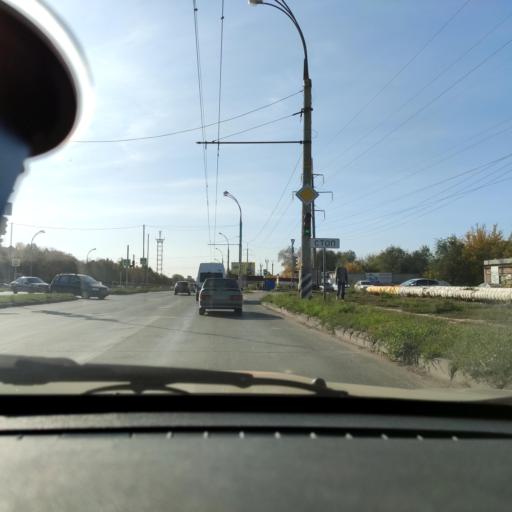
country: RU
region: Samara
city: Tol'yatti
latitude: 53.5373
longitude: 49.2629
